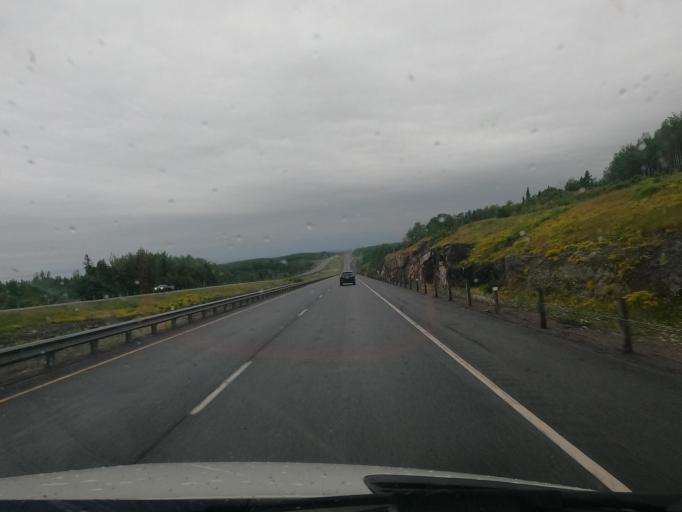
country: CA
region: Ontario
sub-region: Thunder Bay District
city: Thunder Bay
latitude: 48.5035
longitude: -89.1247
